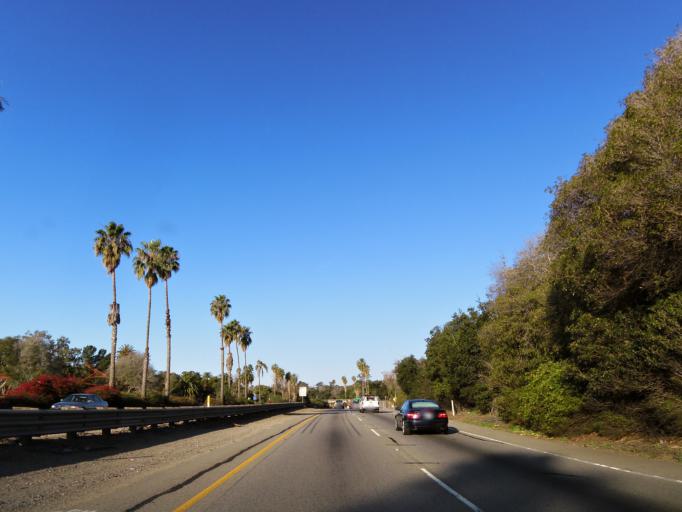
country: US
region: California
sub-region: Santa Barbara County
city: Montecito
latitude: 34.4213
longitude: -119.6279
